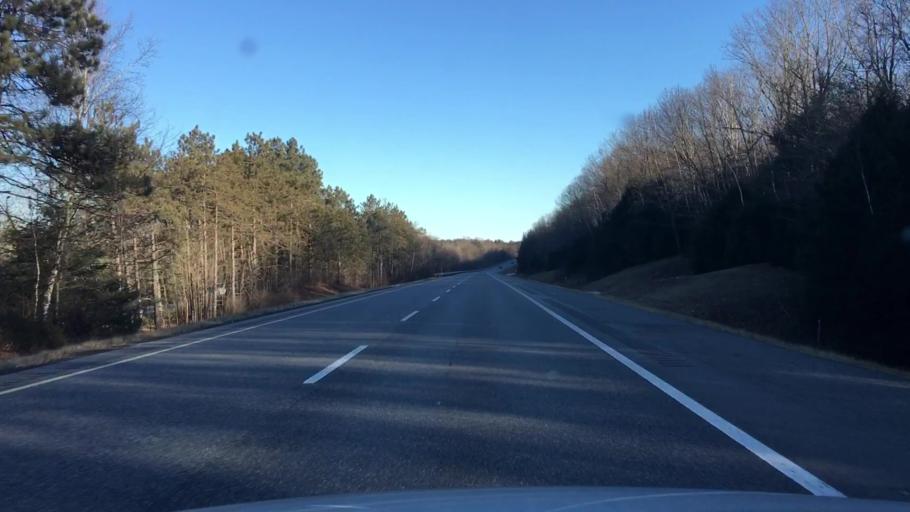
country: US
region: Maine
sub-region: Kennebec County
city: Augusta
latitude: 44.3703
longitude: -69.7740
